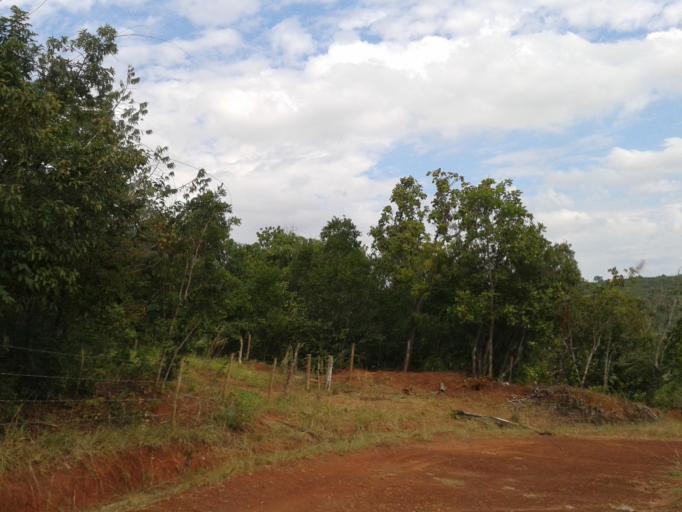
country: BR
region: Minas Gerais
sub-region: Campina Verde
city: Campina Verde
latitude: -19.3944
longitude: -49.6616
